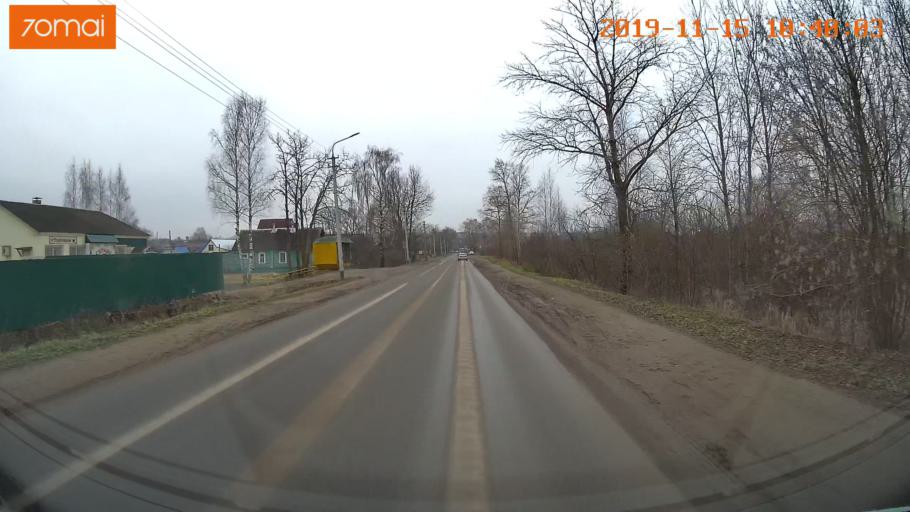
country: RU
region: Vologda
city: Sheksna
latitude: 59.2170
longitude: 38.5103
